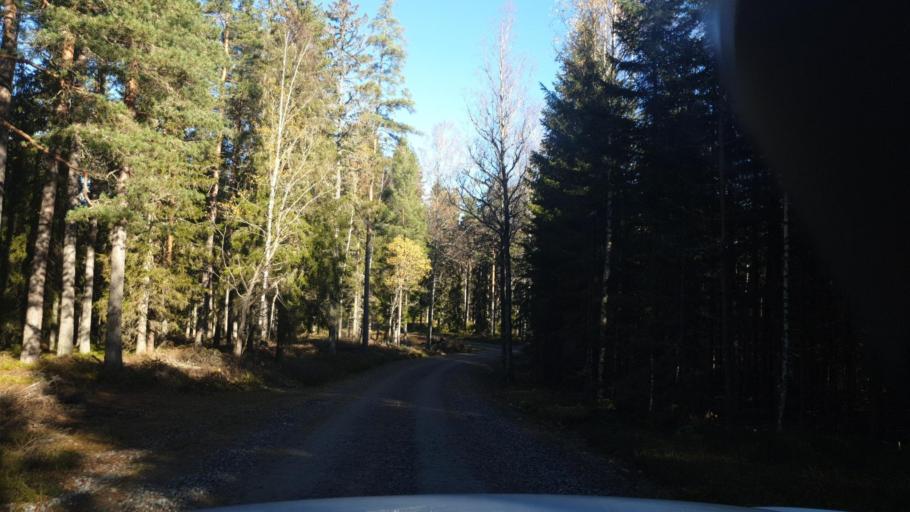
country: SE
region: Vaermland
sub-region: Karlstads Kommun
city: Edsvalla
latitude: 59.4609
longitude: 13.1007
